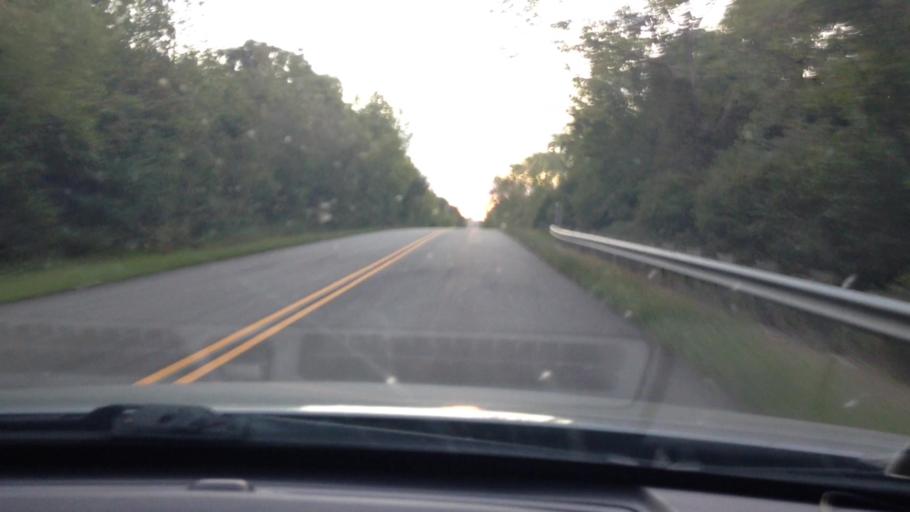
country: US
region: Kansas
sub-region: Leavenworth County
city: Lansing
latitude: 39.1868
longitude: -94.8737
